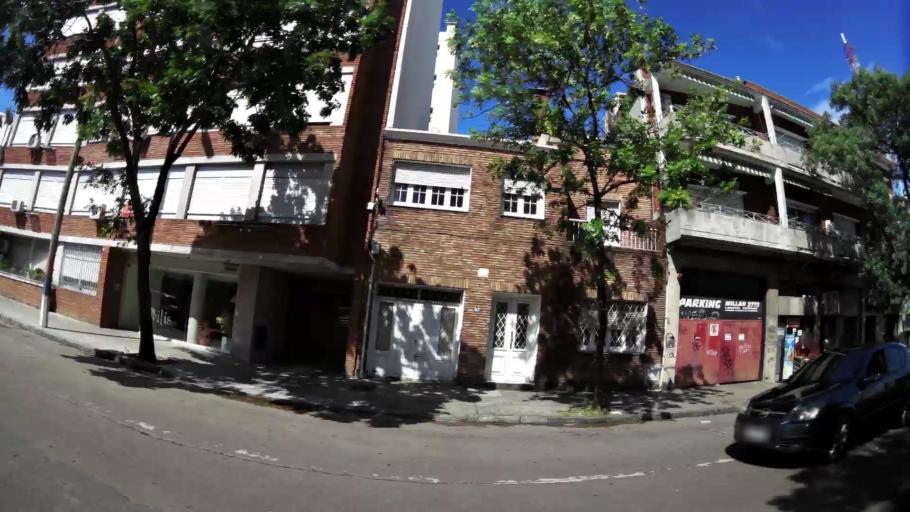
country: UY
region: Montevideo
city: Montevideo
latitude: -34.8757
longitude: -56.1878
